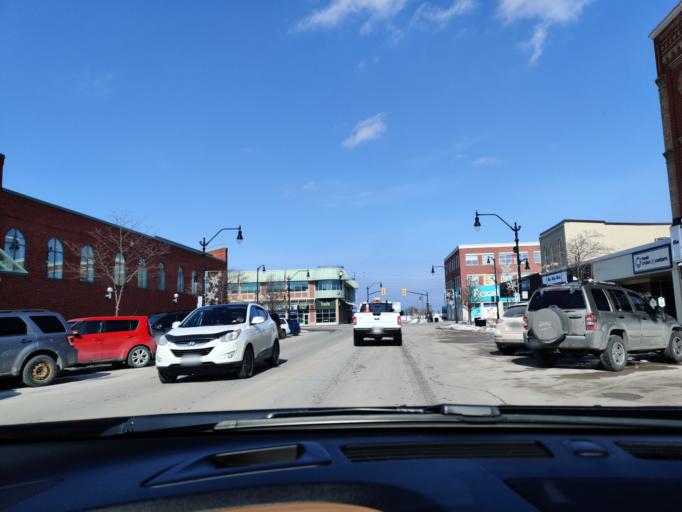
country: CA
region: Ontario
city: Collingwood
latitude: 44.5022
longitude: -80.2173
